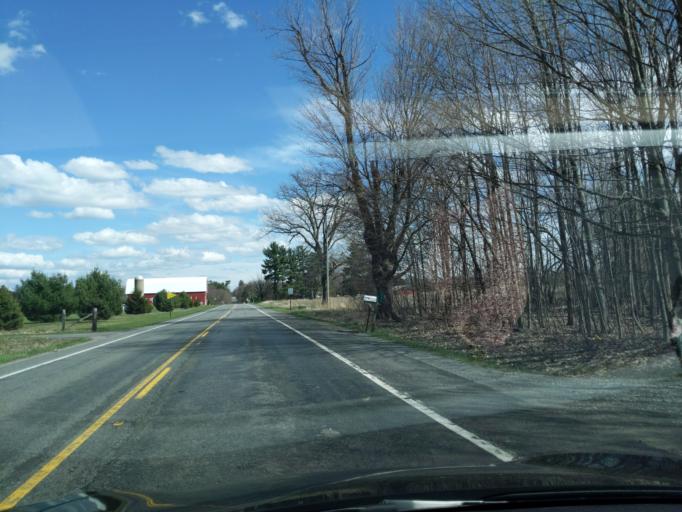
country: US
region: Michigan
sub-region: Ingham County
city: Mason
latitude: 42.5538
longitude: -84.3943
